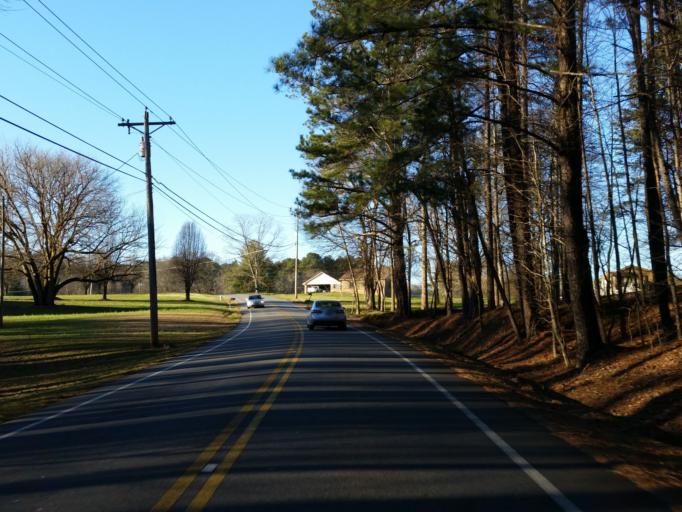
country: US
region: Georgia
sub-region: Cherokee County
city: Holly Springs
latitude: 34.1388
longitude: -84.4547
